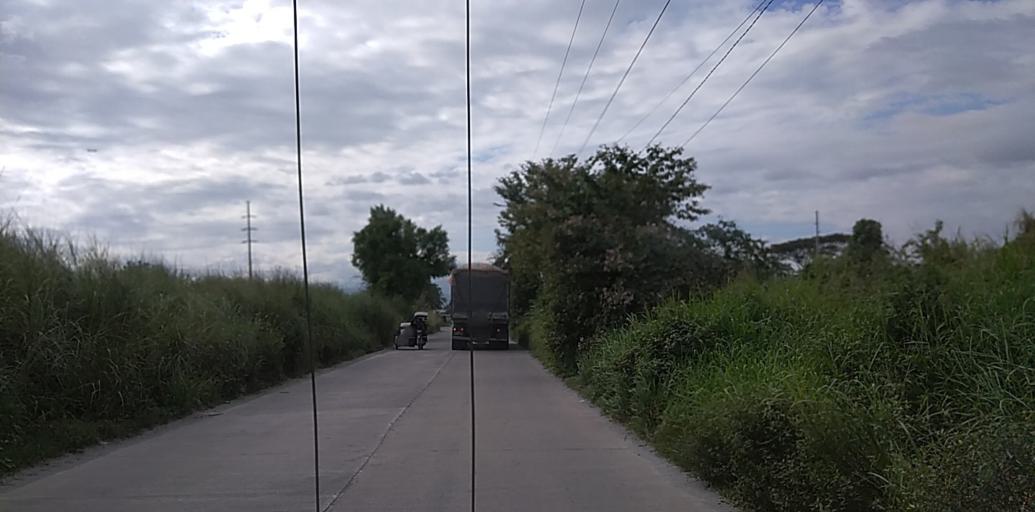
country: PH
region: Central Luzon
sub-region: Province of Pampanga
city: Porac
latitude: 15.0696
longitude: 120.5513
